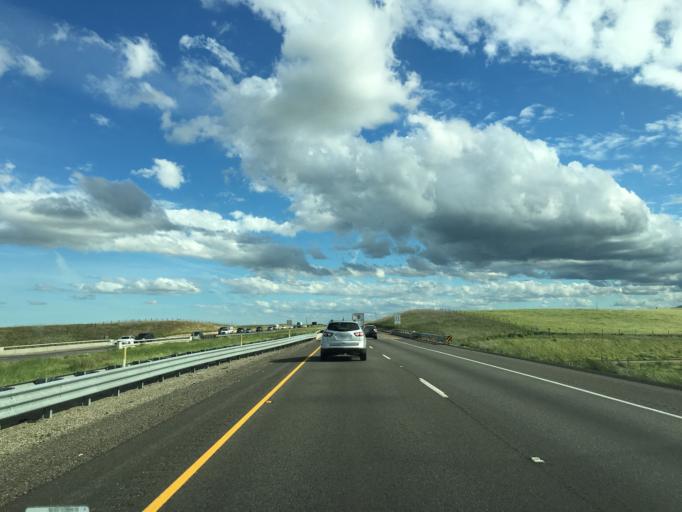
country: US
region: California
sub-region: Merced County
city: Los Banos
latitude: 37.0475
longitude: -120.9612
